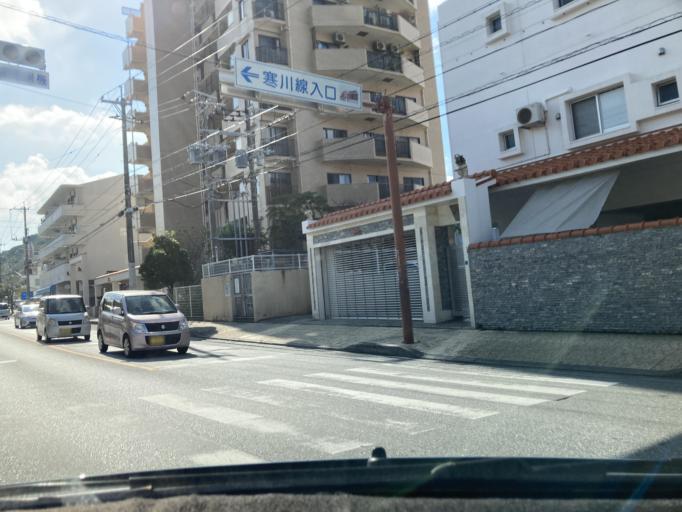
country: JP
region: Okinawa
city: Naha-shi
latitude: 26.2156
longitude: 127.7122
